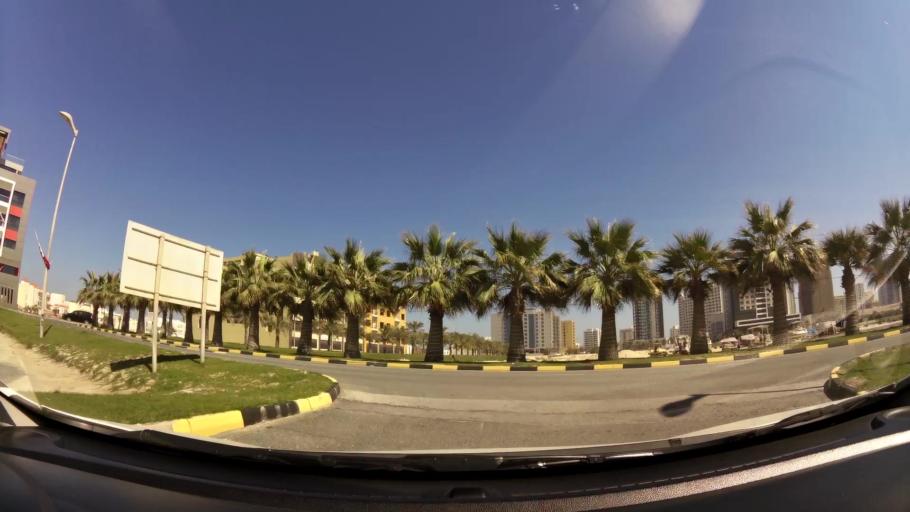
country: BH
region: Muharraq
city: Al Hadd
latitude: 26.2935
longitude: 50.6600
